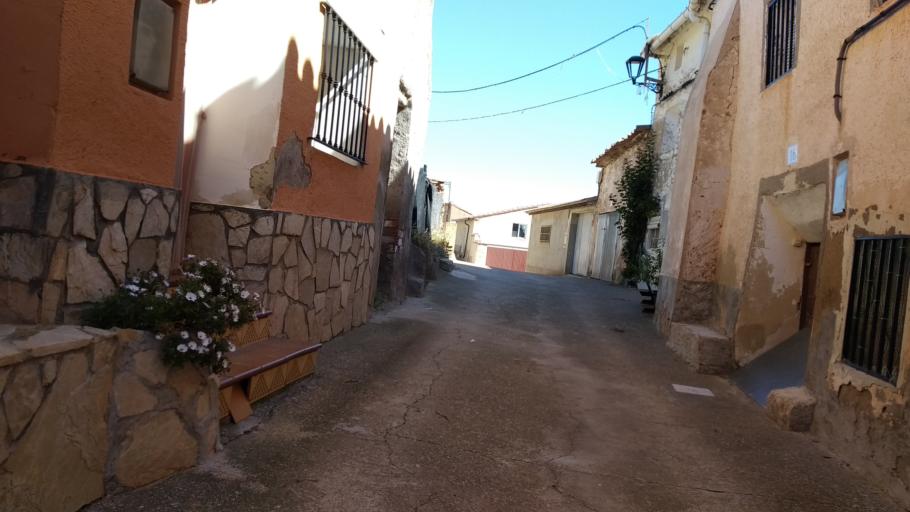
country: ES
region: Aragon
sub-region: Provincia de Teruel
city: Monforte de Moyuela
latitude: 41.0547
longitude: -1.0148
